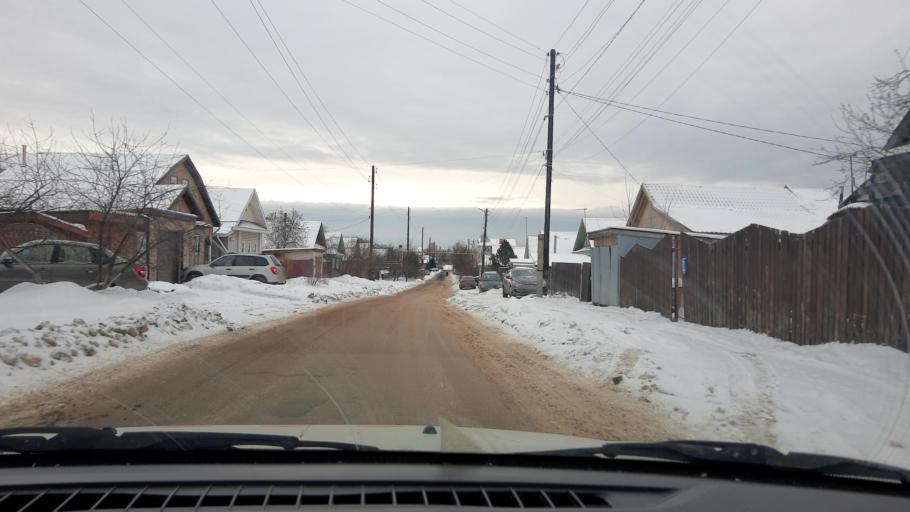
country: RU
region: Nizjnij Novgorod
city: Gorodets
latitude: 56.6606
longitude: 43.4803
